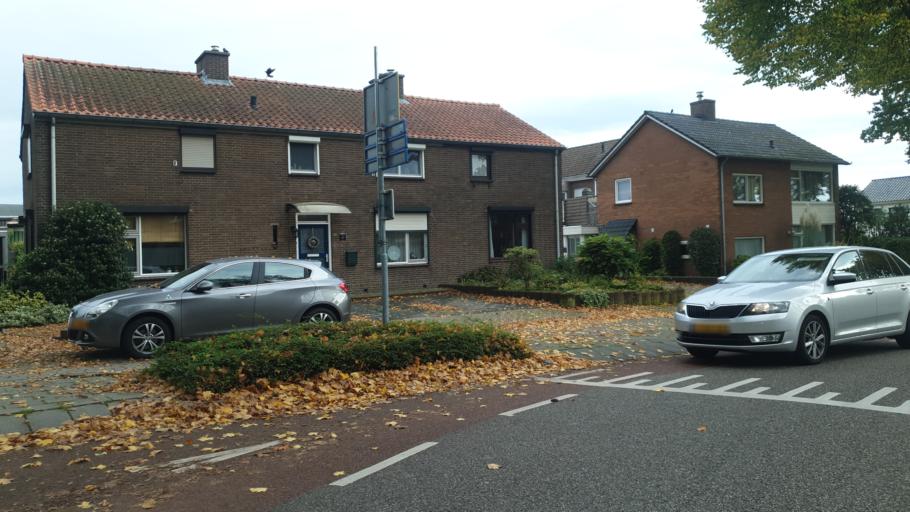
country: NL
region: Gelderland
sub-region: Gemeente Groesbeek
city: Groesbeek
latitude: 51.7754
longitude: 5.9409
